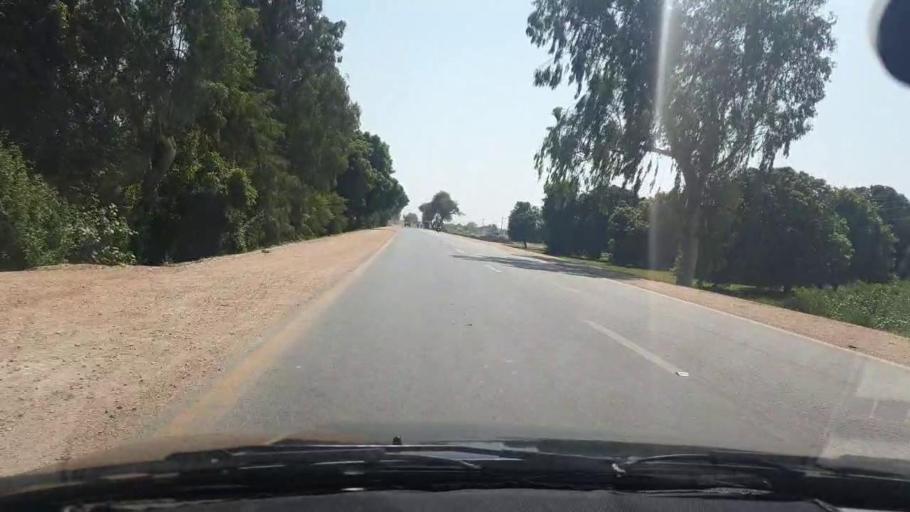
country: PK
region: Sindh
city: Tando Allahyar
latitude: 25.4381
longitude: 68.7398
